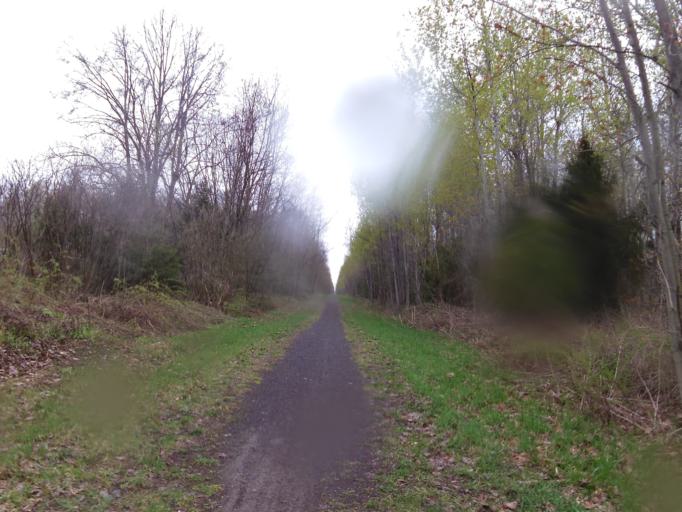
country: CA
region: Ontario
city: Bourget
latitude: 45.4332
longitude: -75.2578
